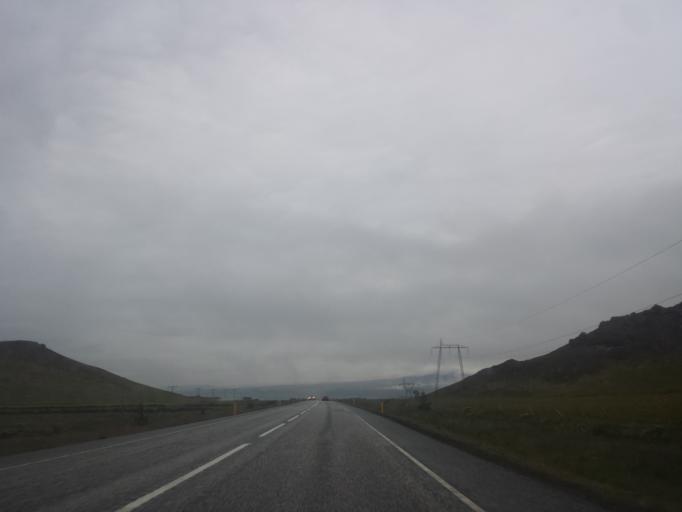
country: IS
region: South
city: Selfoss
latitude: 63.9576
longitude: -21.0702
